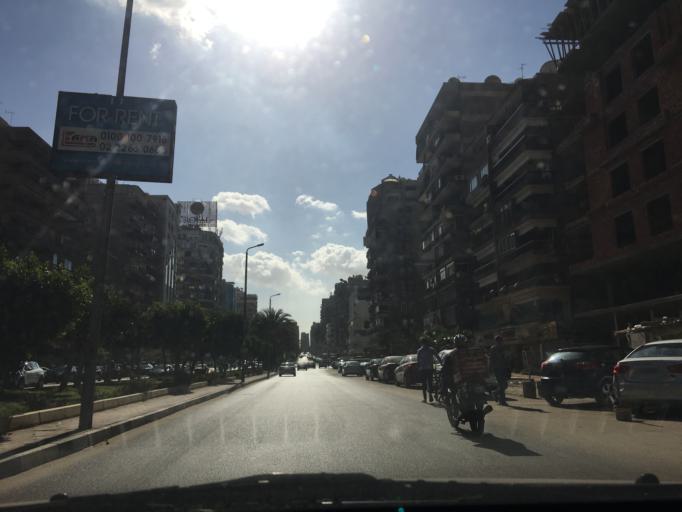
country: EG
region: Muhafazat al Qahirah
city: Cairo
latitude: 30.0563
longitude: 31.3459
